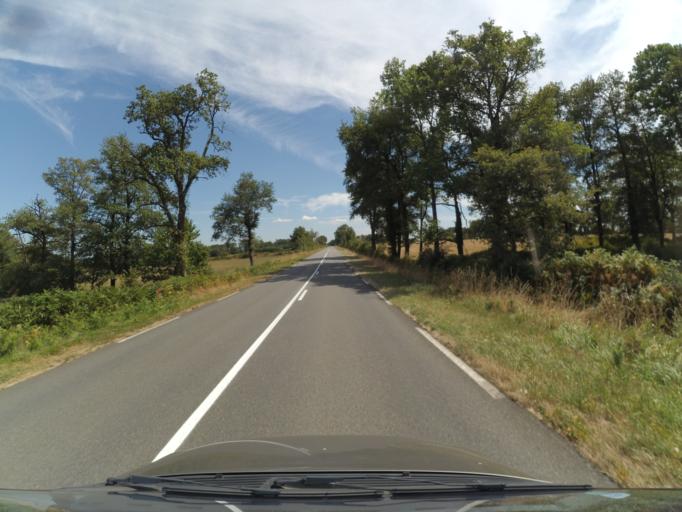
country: FR
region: Poitou-Charentes
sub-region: Departement de la Charente
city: Confolens
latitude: 46.0451
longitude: 0.6236
